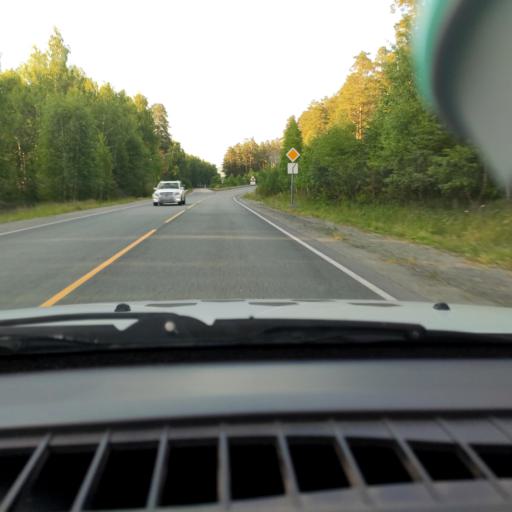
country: RU
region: Chelyabinsk
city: Karabash
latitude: 55.3161
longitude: 60.2142
